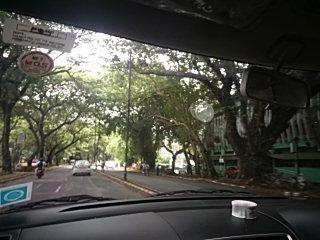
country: IN
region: Goa
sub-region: North Goa
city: Panaji
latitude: 15.4971
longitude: 73.8193
